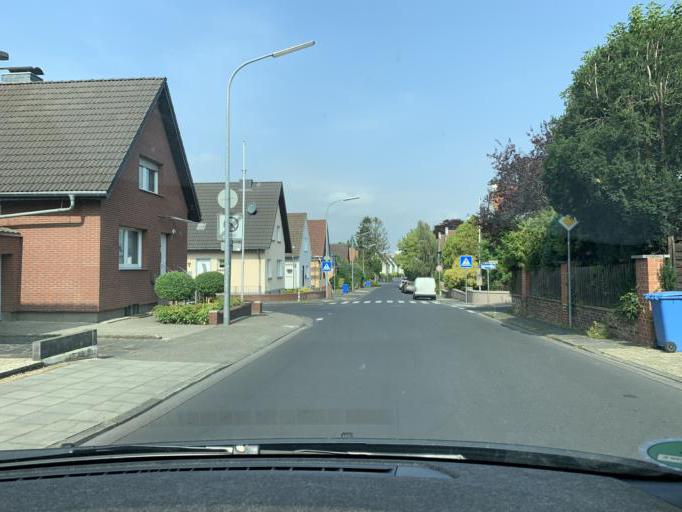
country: DE
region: North Rhine-Westphalia
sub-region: Regierungsbezirk Koln
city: Erftstadt
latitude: 50.8070
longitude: 6.8284
